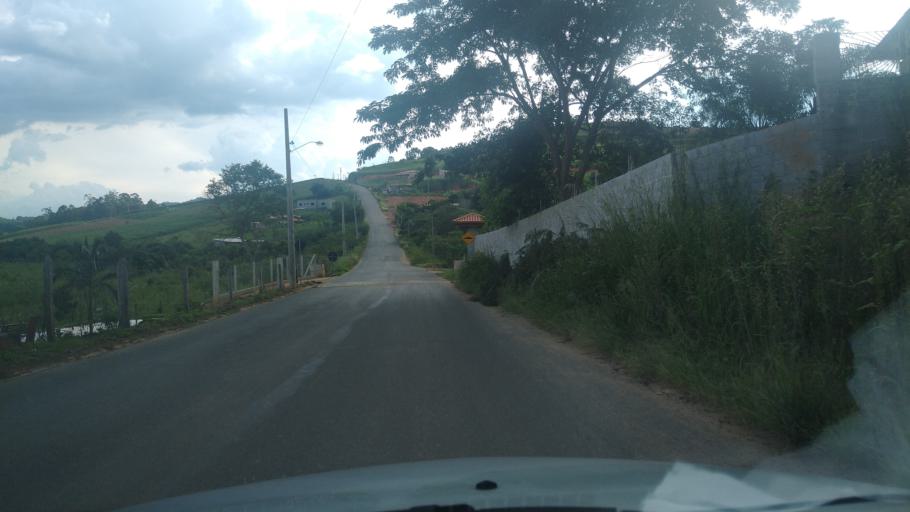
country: BR
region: Minas Gerais
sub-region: Extrema
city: Extrema
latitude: -22.7323
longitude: -46.3631
